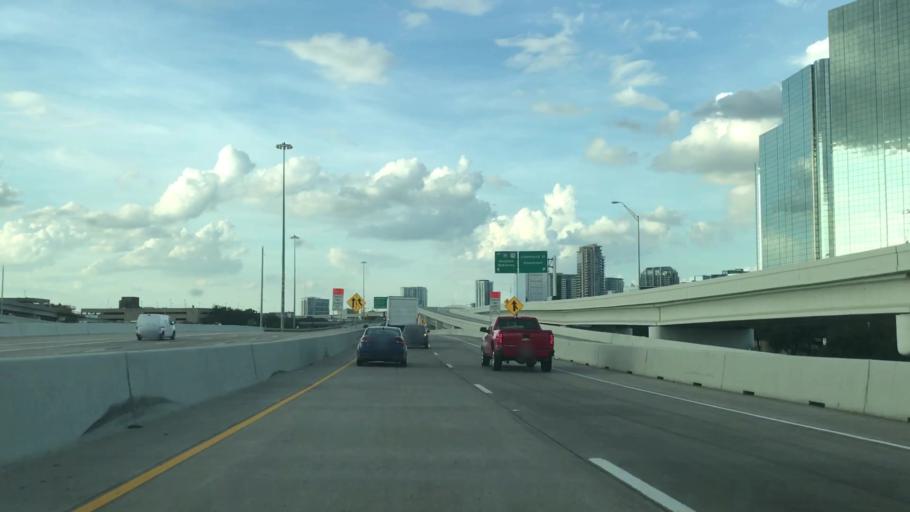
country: US
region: Texas
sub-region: Dallas County
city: Dallas
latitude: 32.7741
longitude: -96.8107
